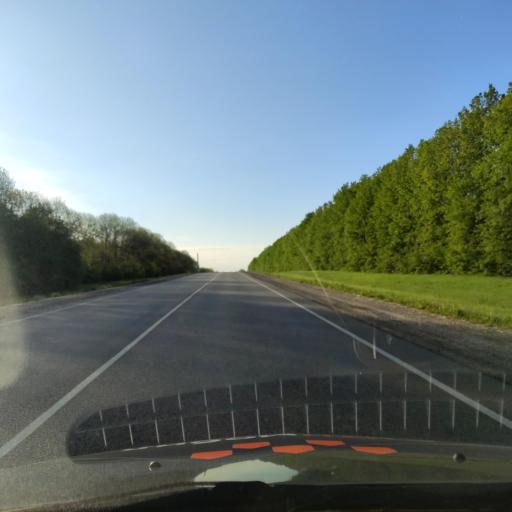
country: RU
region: Lipetsk
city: Yelets
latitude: 52.5691
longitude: 38.6651
